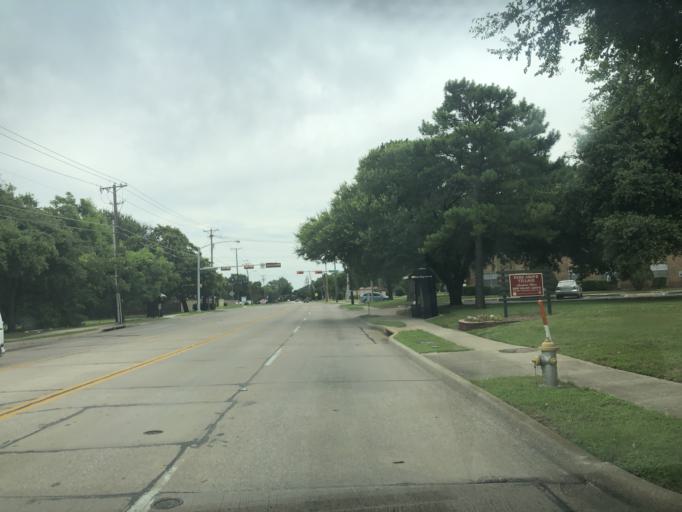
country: US
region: Texas
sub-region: Dallas County
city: Irving
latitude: 32.8024
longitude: -96.9871
